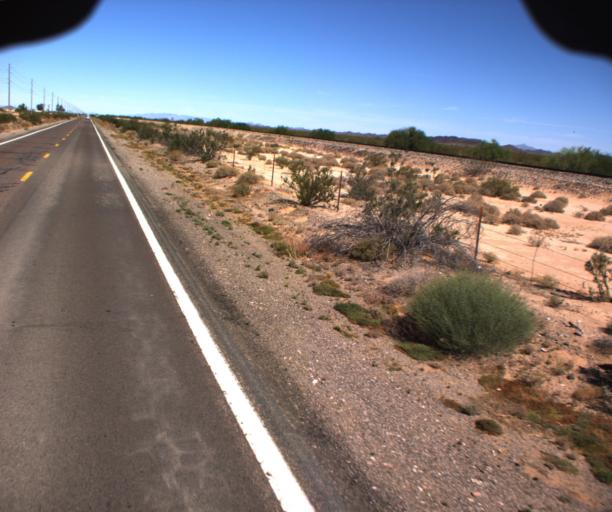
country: US
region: Arizona
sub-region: La Paz County
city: Salome
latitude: 33.8598
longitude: -113.9165
